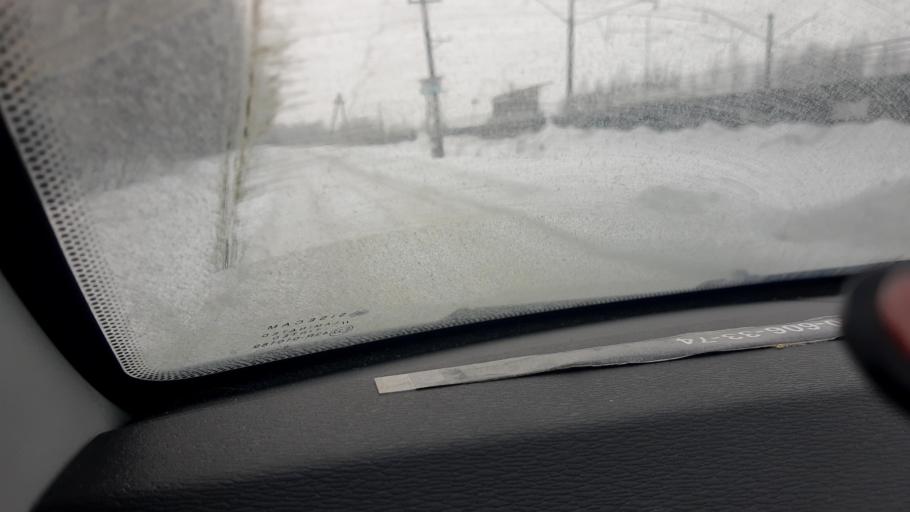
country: RU
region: Nizjnij Novgorod
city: Sitniki
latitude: 56.5220
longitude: 44.0511
